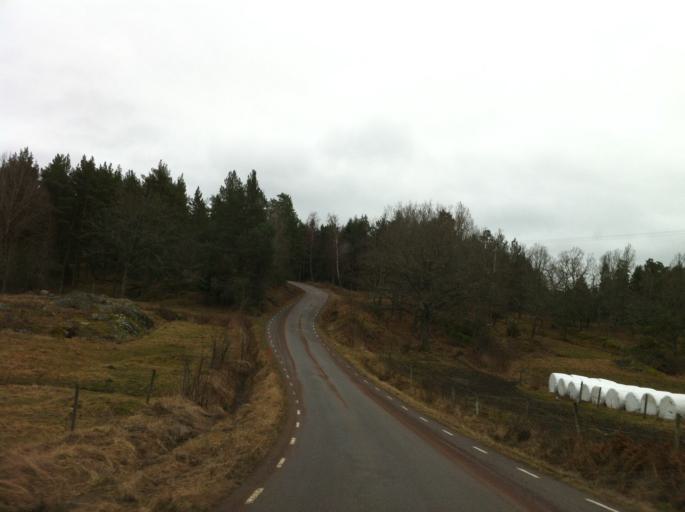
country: SE
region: Kalmar
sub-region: Vasterviks Kommun
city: Forserum
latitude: 57.9190
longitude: 16.5994
